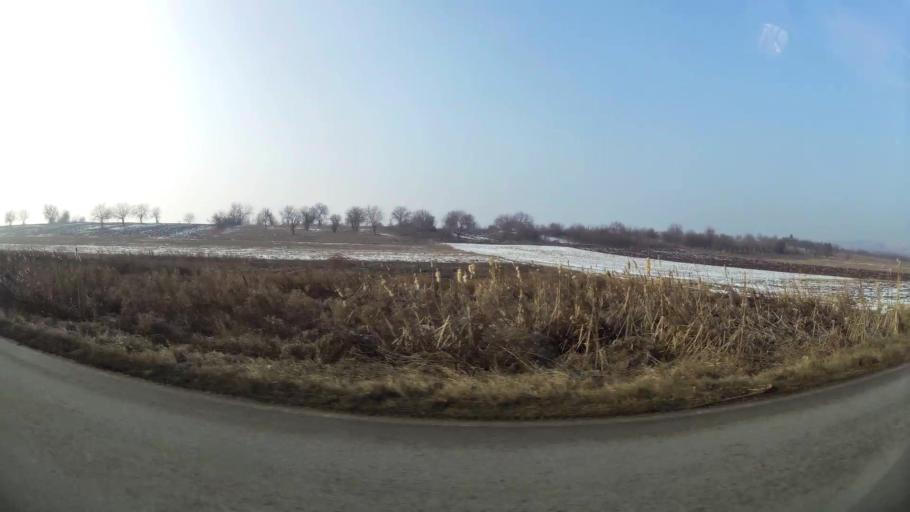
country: MK
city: Kadino
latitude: 41.9752
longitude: 21.6095
